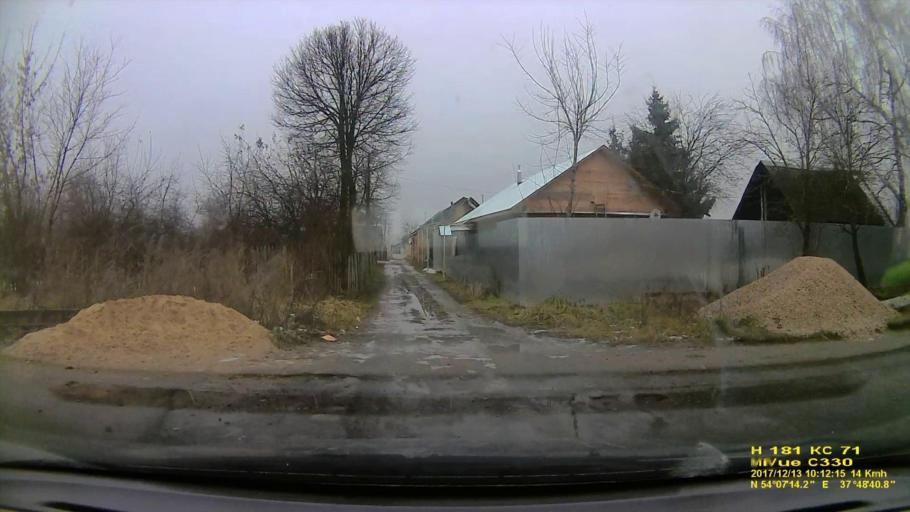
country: RU
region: Tula
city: Bolokhovo
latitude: 54.1206
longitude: 37.8113
